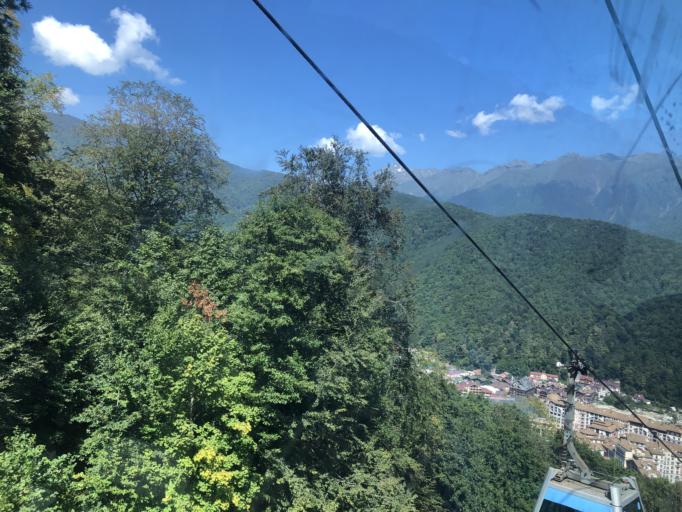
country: RU
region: Krasnodarskiy
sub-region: Sochi City
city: Krasnaya Polyana
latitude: 43.6782
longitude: 40.2642
